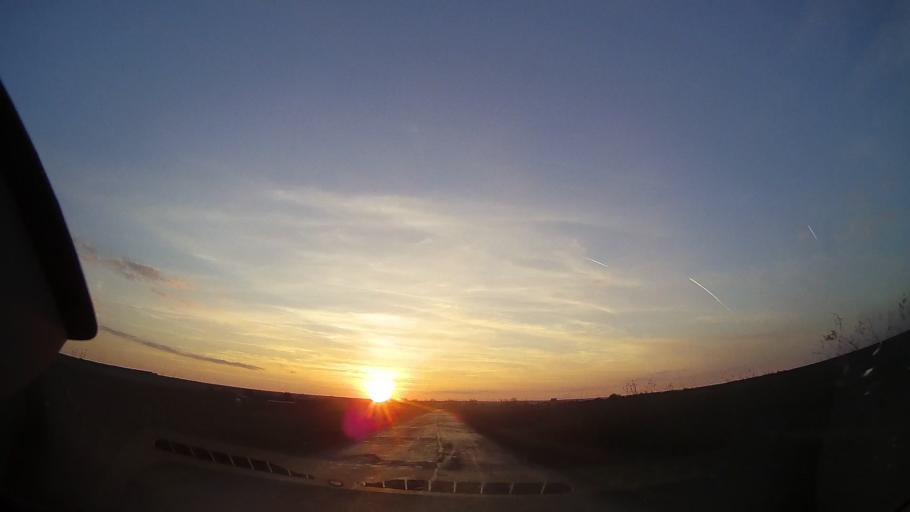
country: RO
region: Constanta
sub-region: Comuna Mereni
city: Mereni
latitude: 44.0172
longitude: 28.3371
